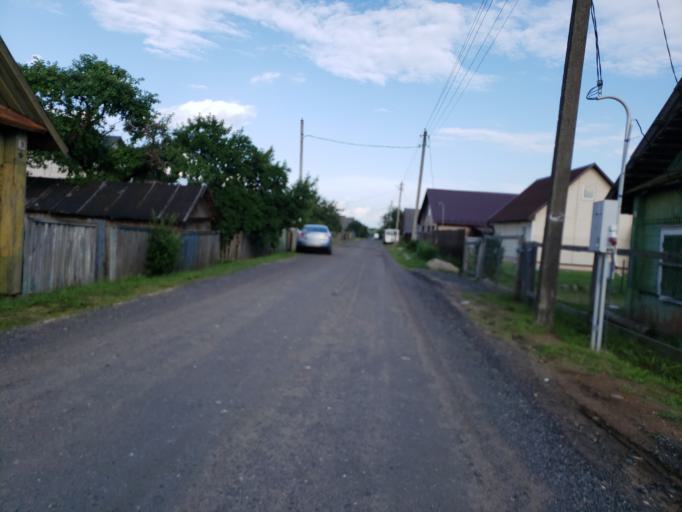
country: BY
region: Minsk
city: Chervyen'
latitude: 53.7076
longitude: 28.4228
